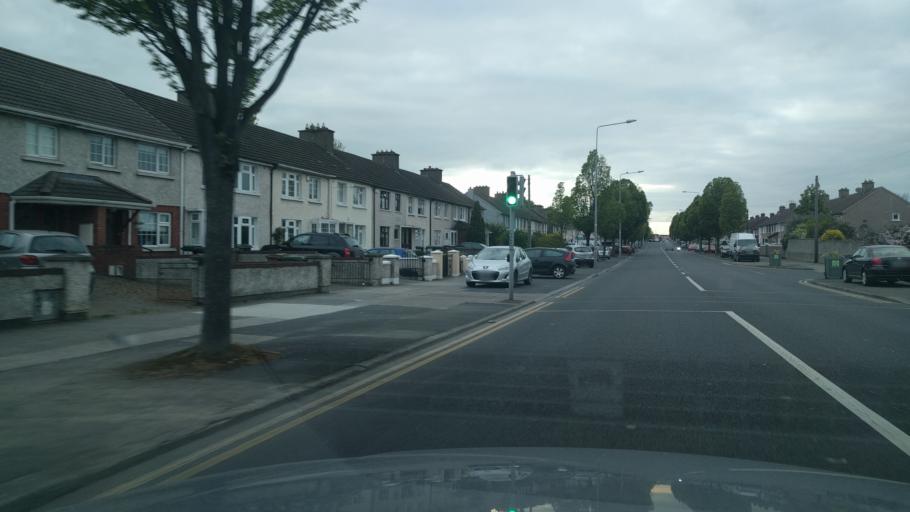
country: IE
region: Leinster
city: Crumlin
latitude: 53.3195
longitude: -6.3366
